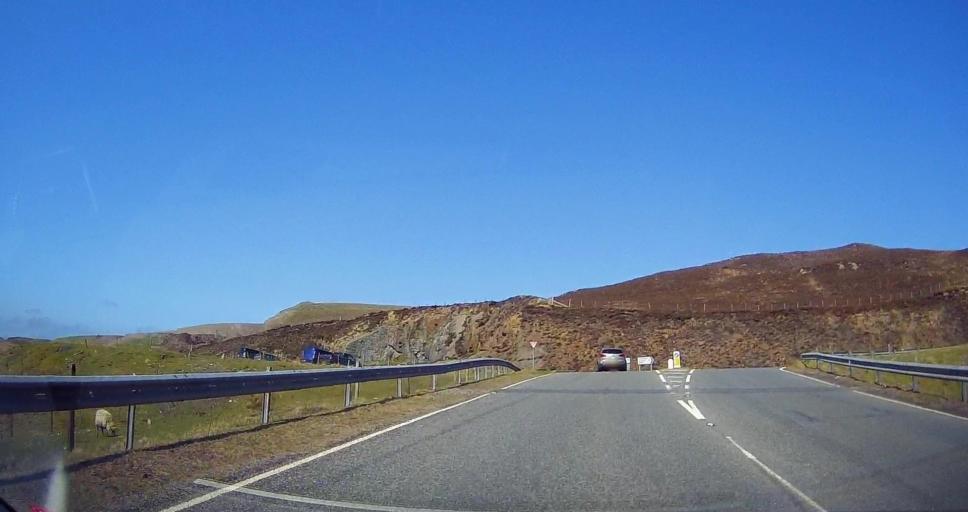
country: GB
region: Scotland
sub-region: Shetland Islands
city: Lerwick
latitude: 60.1420
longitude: -1.2459
